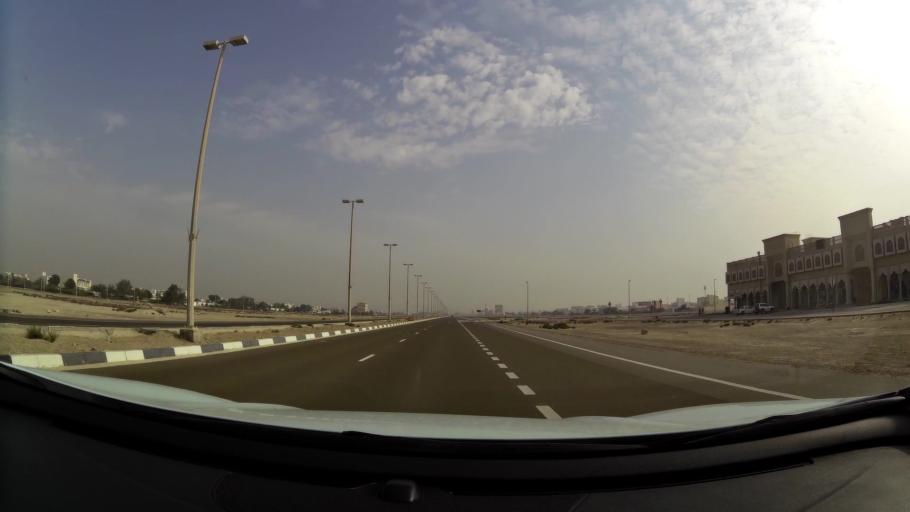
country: AE
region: Abu Dhabi
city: Abu Dhabi
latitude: 24.6603
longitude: 54.7648
